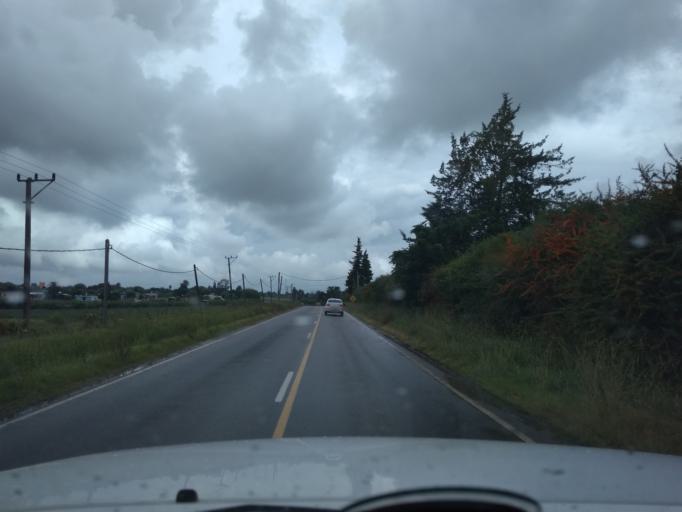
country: UY
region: Canelones
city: Pando
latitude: -34.6807
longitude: -55.9678
